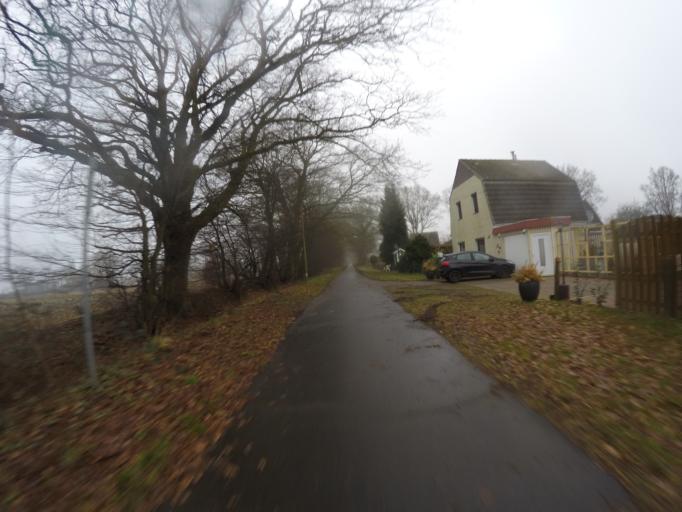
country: DE
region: Schleswig-Holstein
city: Quickborn
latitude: 53.7095
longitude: 9.9139
